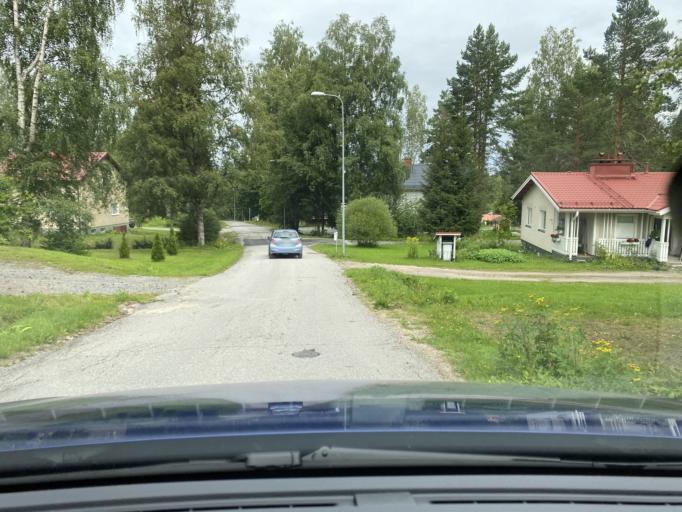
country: FI
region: Pirkanmaa
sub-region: Ylae-Pirkanmaa
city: Maenttae
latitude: 62.0242
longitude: 24.7165
